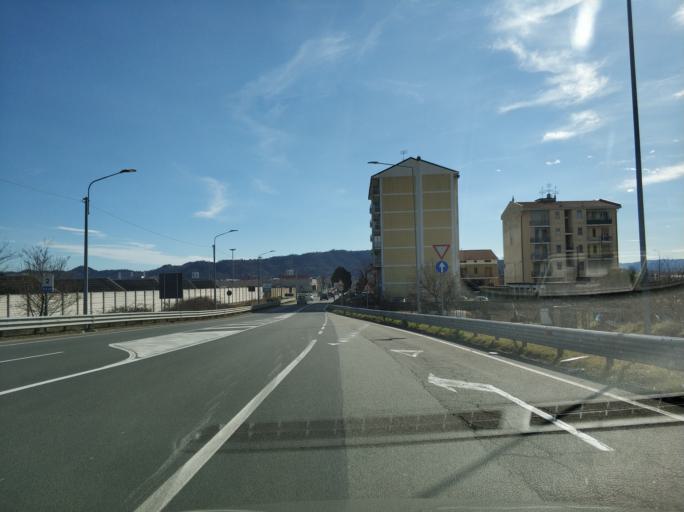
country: IT
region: Piedmont
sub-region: Provincia di Torino
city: Chivasso
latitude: 45.2064
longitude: 7.8900
